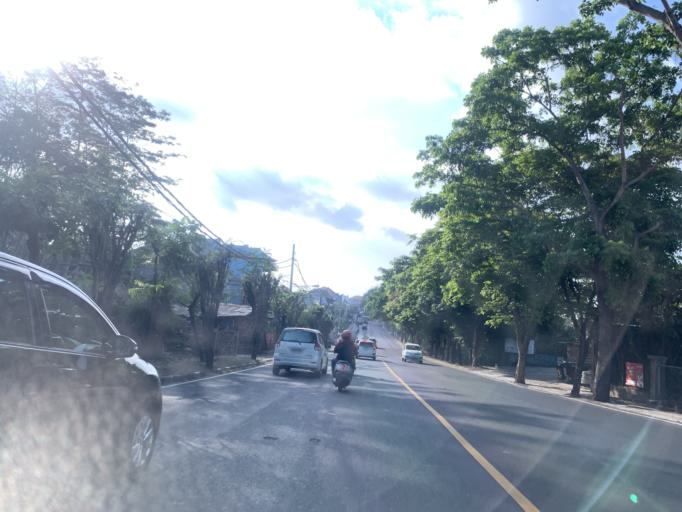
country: ID
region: Bali
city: Banjar Tegal Belodan
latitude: -8.5470
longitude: 115.1178
